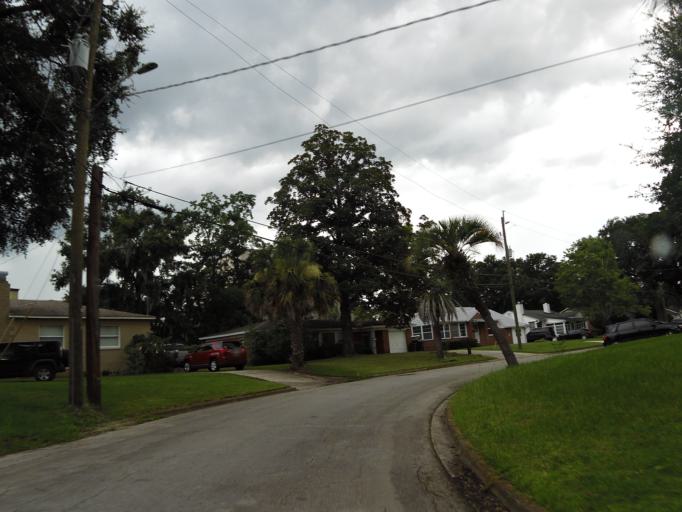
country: US
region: Florida
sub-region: Duval County
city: Jacksonville
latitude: 30.3011
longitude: -81.6374
